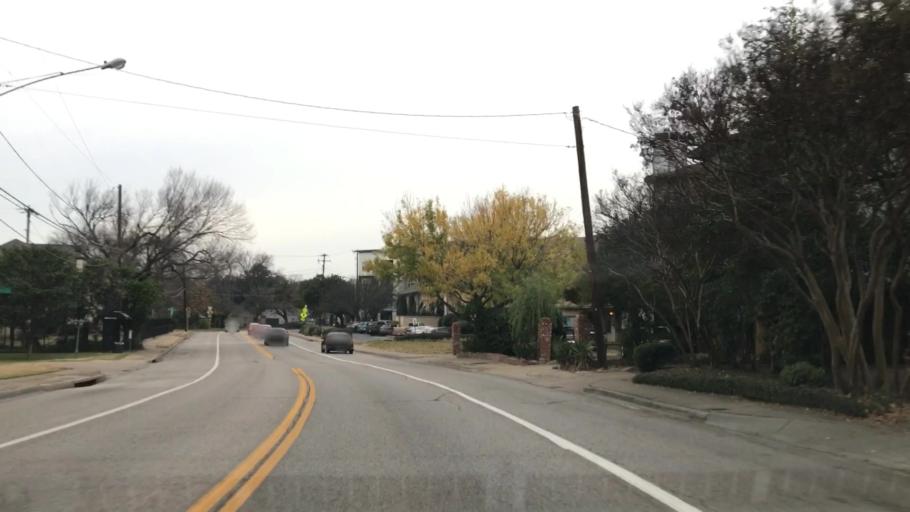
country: US
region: Texas
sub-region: Dallas County
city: Highland Park
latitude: 32.8214
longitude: -96.8239
